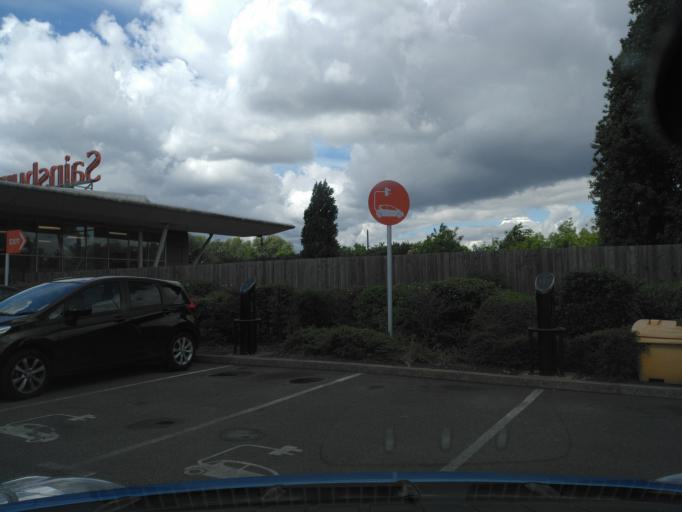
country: GB
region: England
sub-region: Greater London
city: East Ham
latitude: 51.5222
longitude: 0.0656
